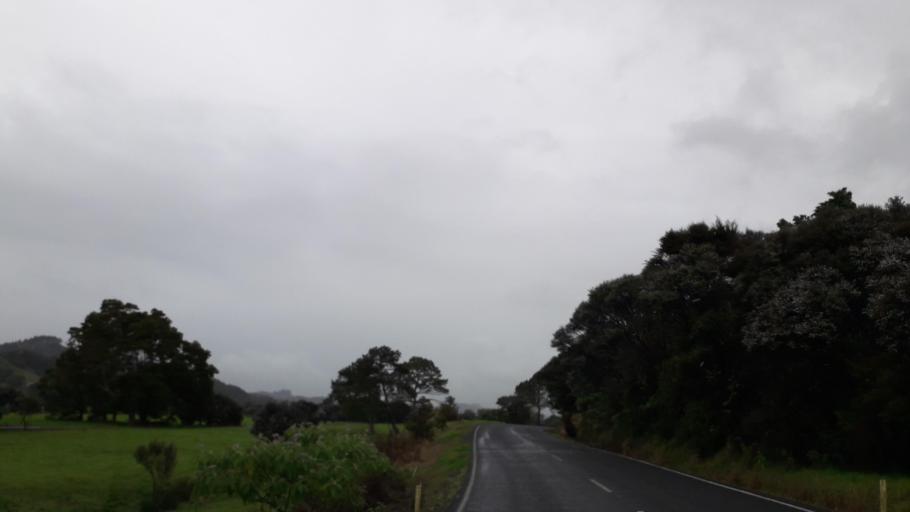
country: NZ
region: Northland
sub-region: Far North District
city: Kaitaia
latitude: -35.3651
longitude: 173.4961
